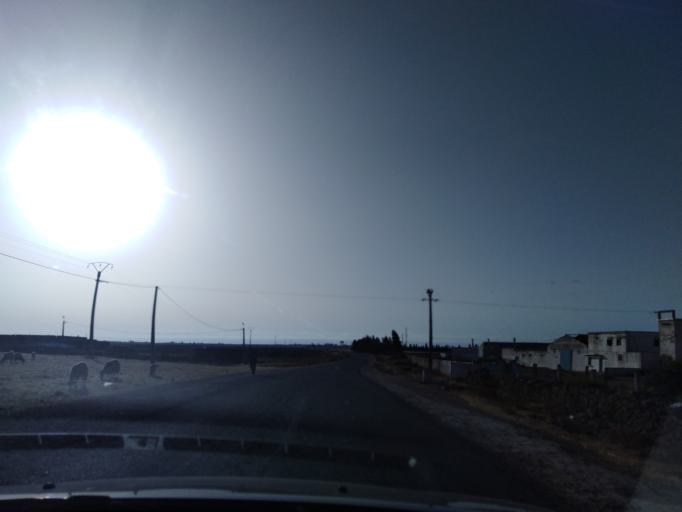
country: MA
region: Doukkala-Abda
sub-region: Safi
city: Safi
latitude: 32.4888
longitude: -8.9209
